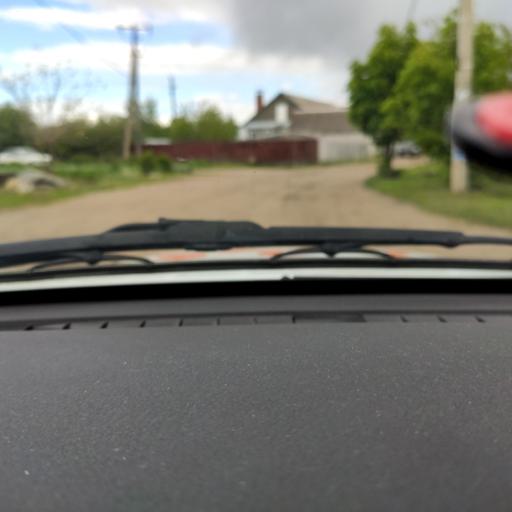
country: RU
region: Voronezj
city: Podgornoye
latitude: 51.7425
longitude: 39.1546
